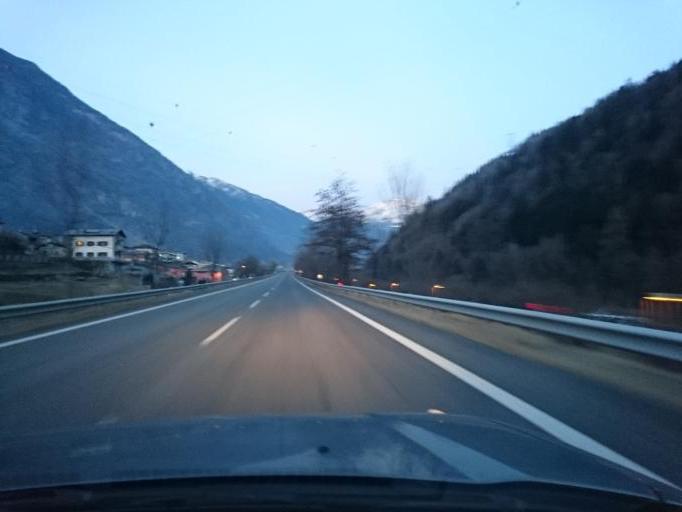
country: IT
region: Lombardy
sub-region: Provincia di Sondrio
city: Grosio
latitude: 46.2948
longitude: 10.2753
